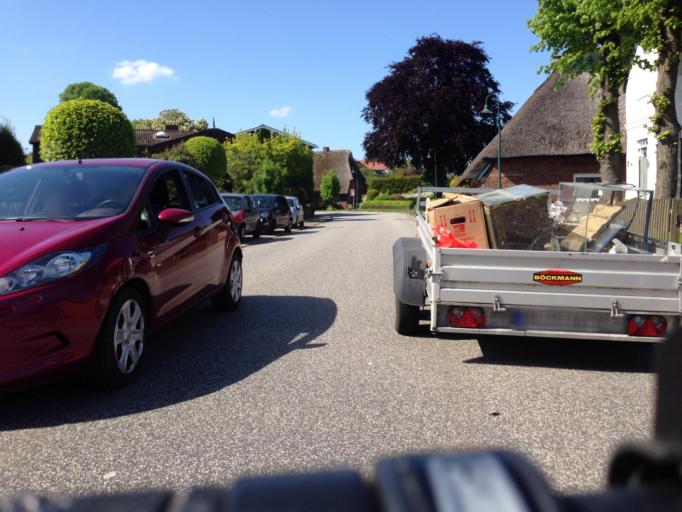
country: DE
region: Schleswig-Holstein
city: Stapelfeld
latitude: 53.6042
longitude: 10.2219
